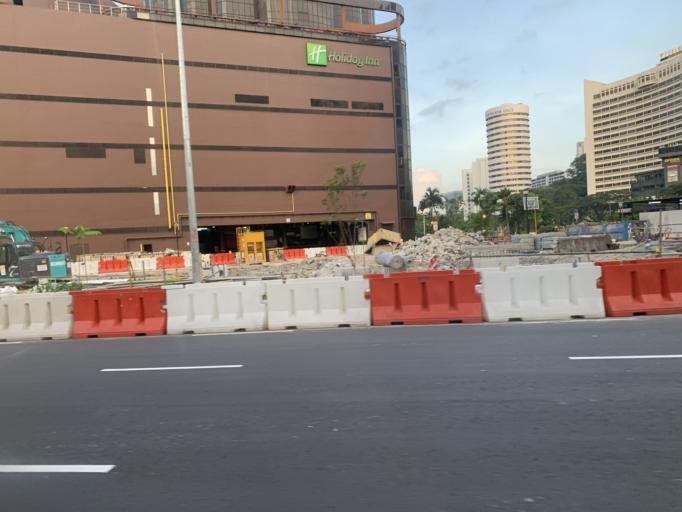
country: SG
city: Singapore
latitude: 1.2884
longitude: 103.8337
